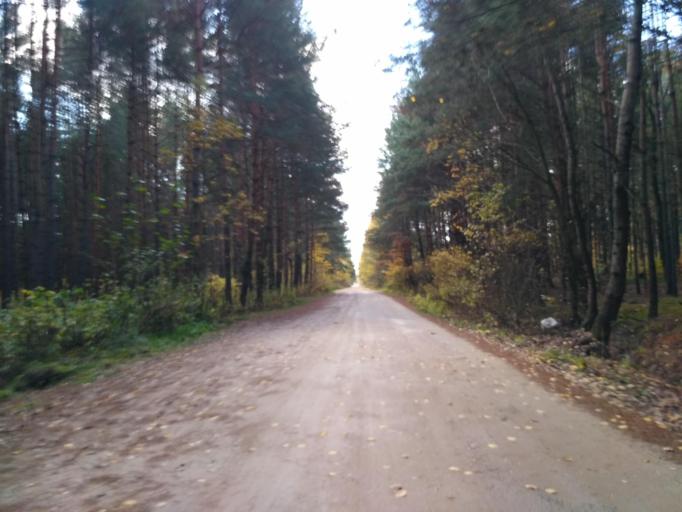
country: PL
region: Subcarpathian Voivodeship
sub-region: Powiat rzeszowski
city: Glogow Malopolski
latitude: 50.1358
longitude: 21.9300
